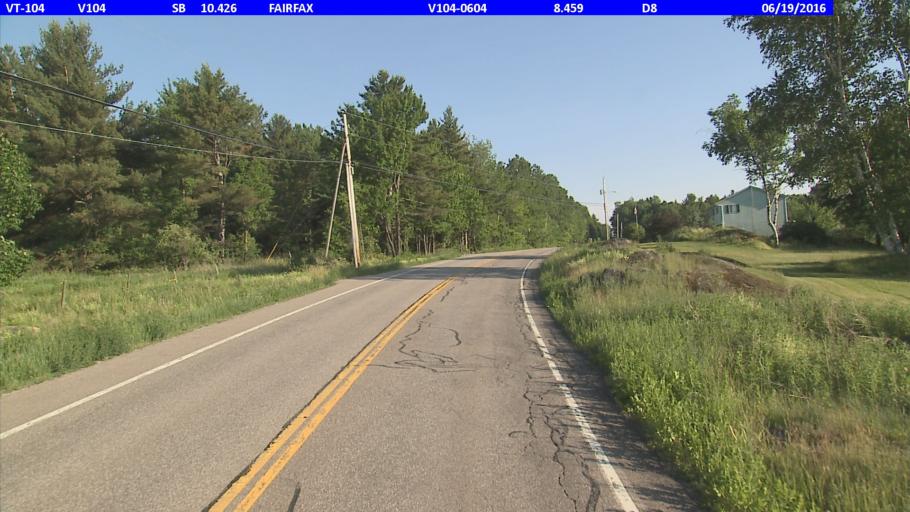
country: US
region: Vermont
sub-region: Chittenden County
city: Milton
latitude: 44.7064
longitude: -73.0365
